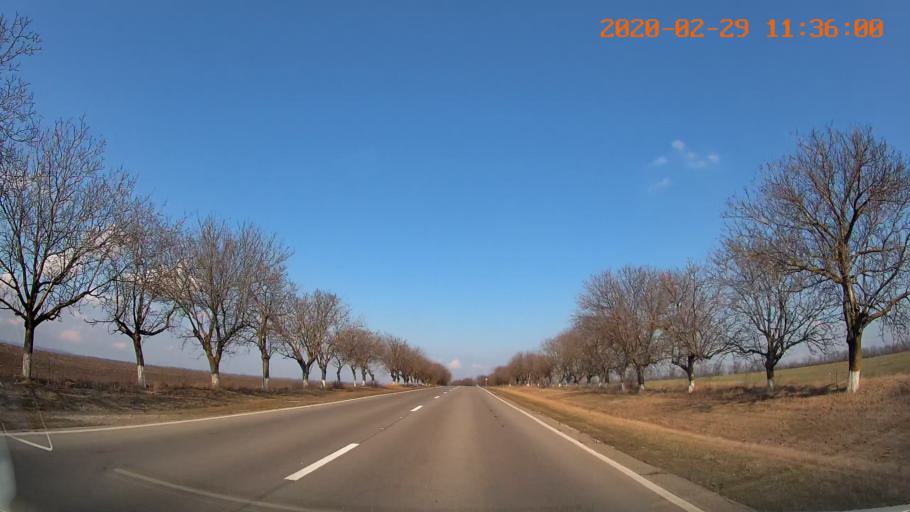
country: MD
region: Rezina
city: Saharna
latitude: 47.5892
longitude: 29.0596
